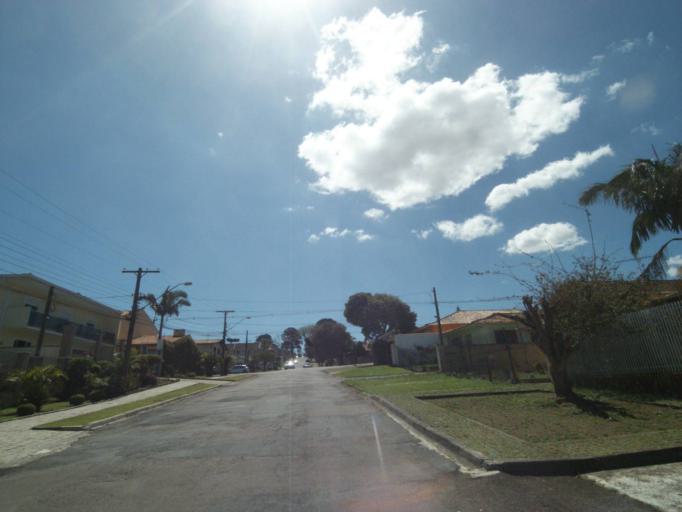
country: BR
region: Parana
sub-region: Curitiba
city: Curitiba
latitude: -25.3915
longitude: -49.2471
